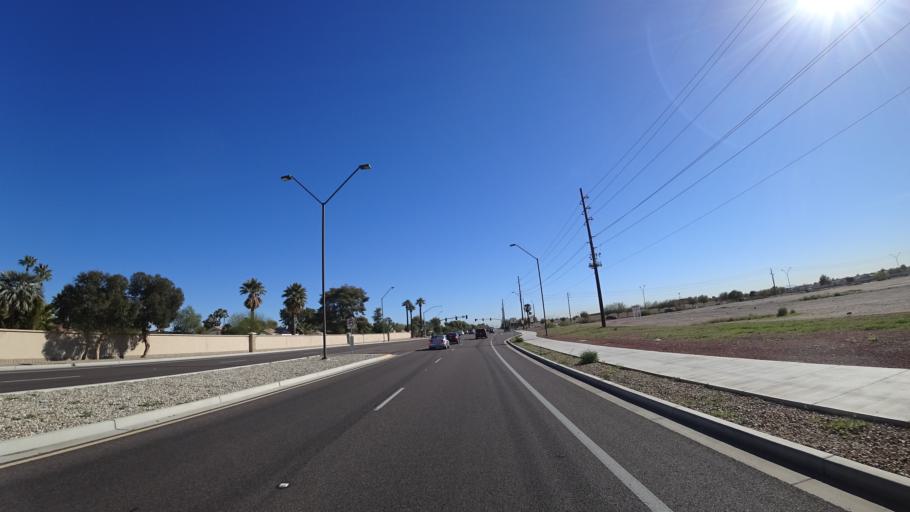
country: US
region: Arizona
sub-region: Maricopa County
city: Litchfield Park
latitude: 33.4932
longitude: -112.3426
